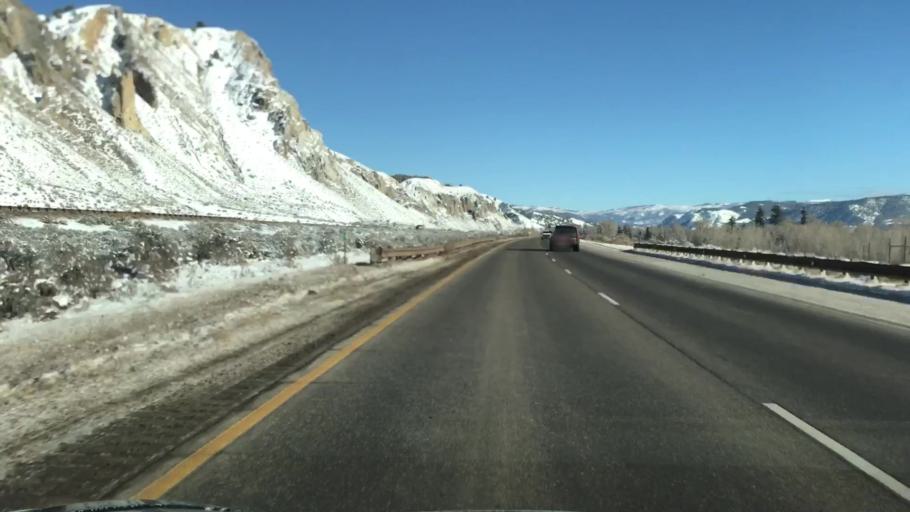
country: US
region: Colorado
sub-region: Eagle County
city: Gypsum
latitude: 39.6538
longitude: -106.9223
